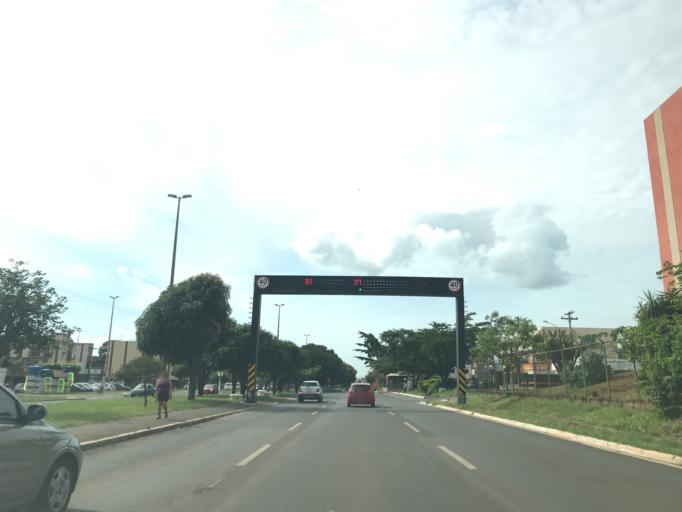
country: BR
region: Federal District
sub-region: Brasilia
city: Brasilia
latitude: -15.8126
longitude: -48.0894
